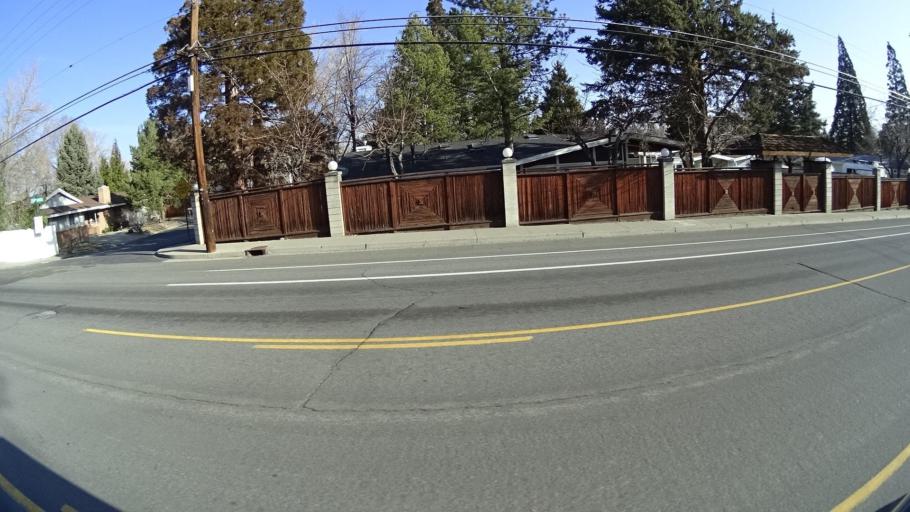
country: US
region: Nevada
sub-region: Washoe County
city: Reno
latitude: 39.5055
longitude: -119.8224
